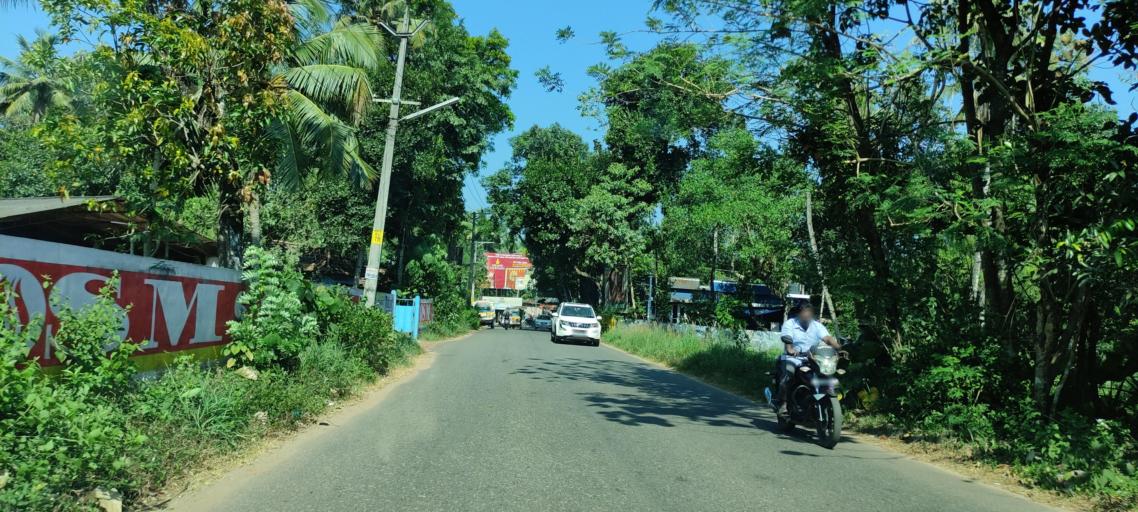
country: IN
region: Kerala
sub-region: Kollam
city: Panmana
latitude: 9.0474
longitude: 76.5752
